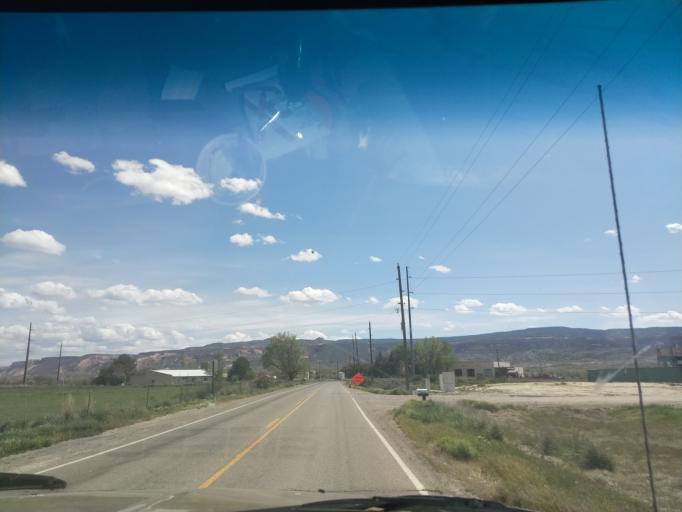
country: US
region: Colorado
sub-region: Mesa County
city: Fruita
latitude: 39.1693
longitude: -108.7571
